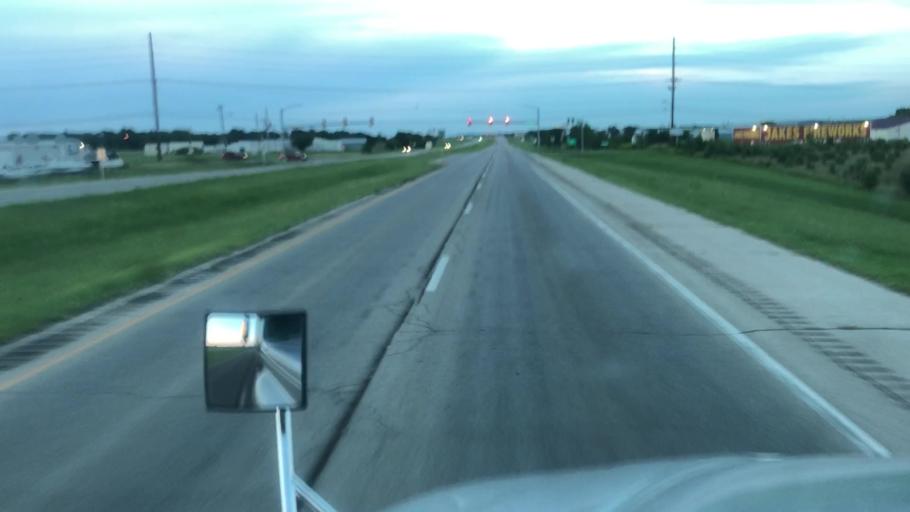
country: US
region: Oklahoma
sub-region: Kay County
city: Ponca City
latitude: 36.7515
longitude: -97.0664
